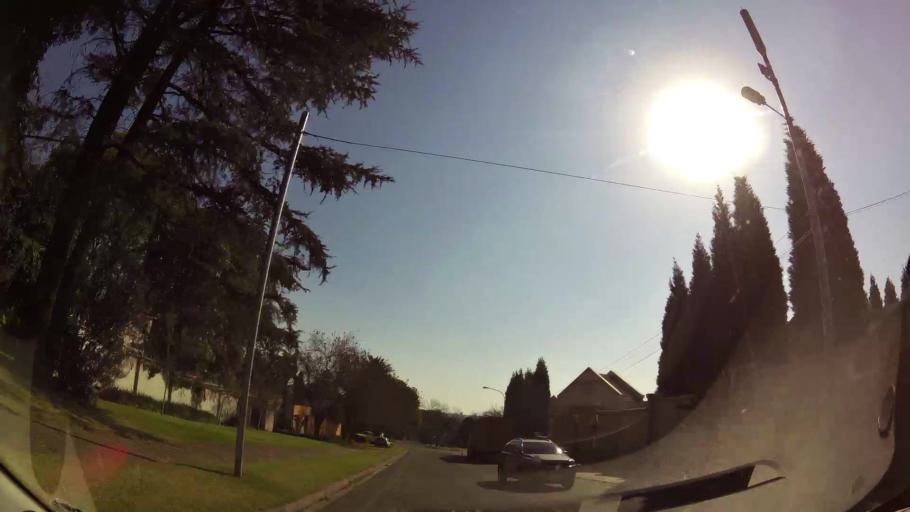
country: ZA
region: Gauteng
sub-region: City of Johannesburg Metropolitan Municipality
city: Johannesburg
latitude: -26.1368
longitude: 28.0313
